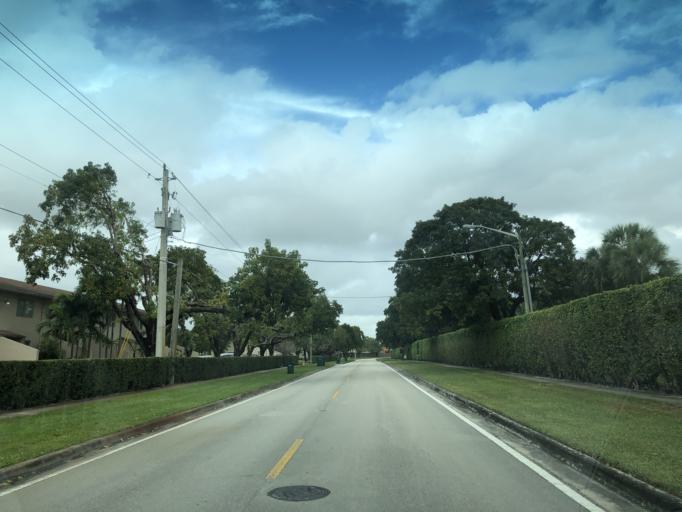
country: US
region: Florida
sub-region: Broward County
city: Margate
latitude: 26.2485
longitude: -80.2322
